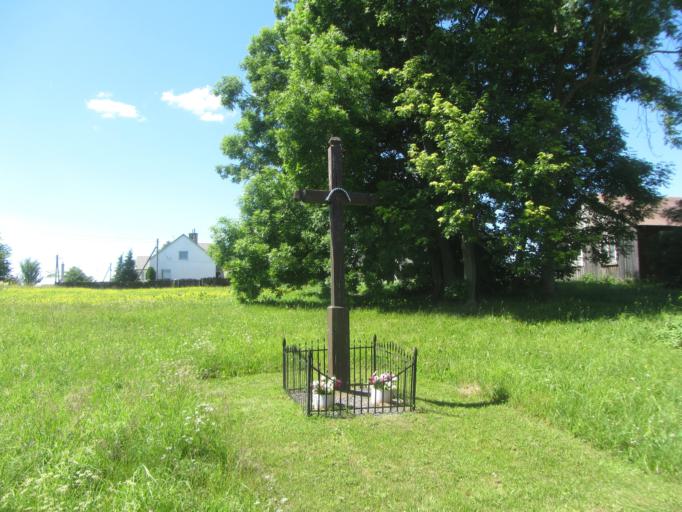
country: LT
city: Jieznas
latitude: 54.7009
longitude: 24.2208
